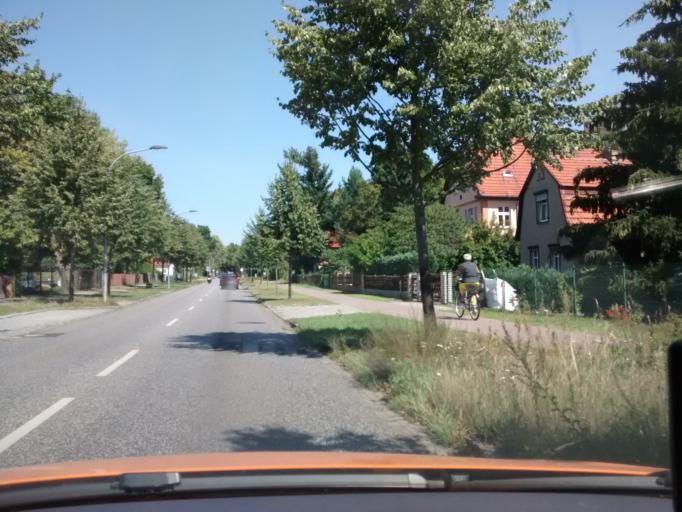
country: DE
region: Brandenburg
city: Birkenwerder
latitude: 52.6822
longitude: 13.2818
